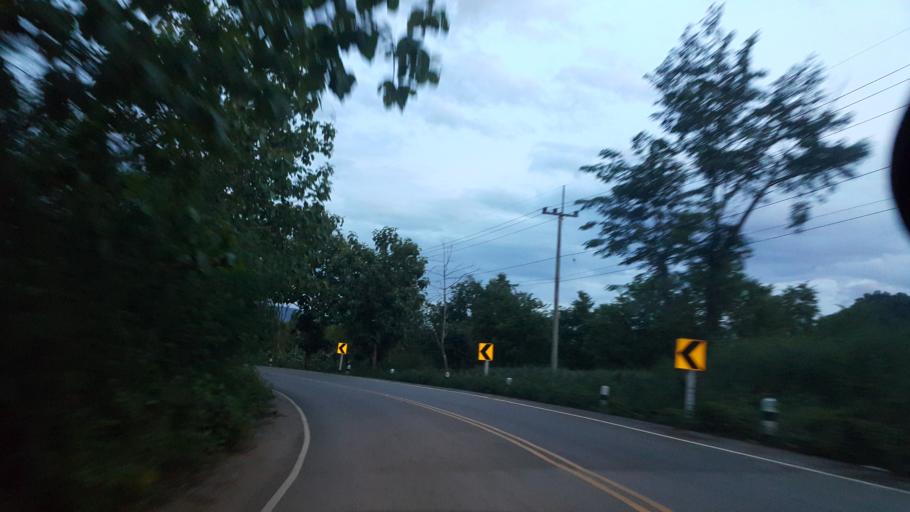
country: TH
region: Loei
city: Phu Ruea
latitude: 17.5312
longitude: 101.2289
